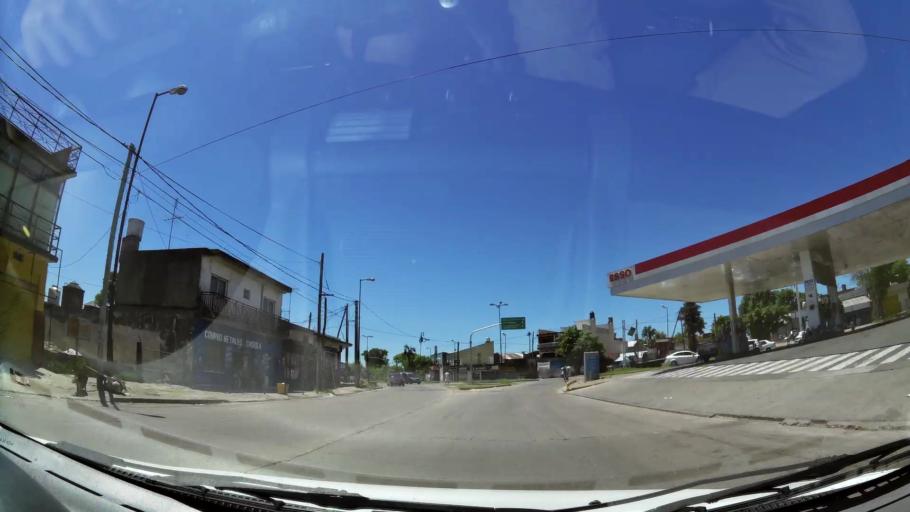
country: AR
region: Buenos Aires
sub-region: Partido de Tigre
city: Tigre
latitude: -34.4970
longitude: -58.5822
